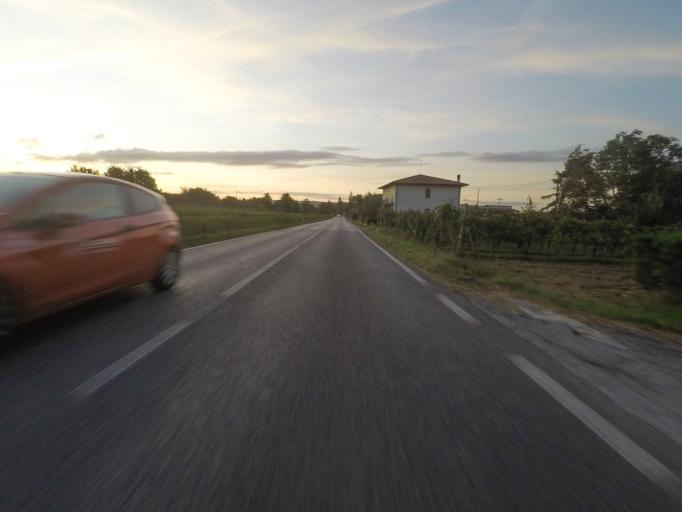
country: IT
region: Tuscany
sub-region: Provincia di Siena
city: Torrita di Siena
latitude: 43.1840
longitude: 11.7684
